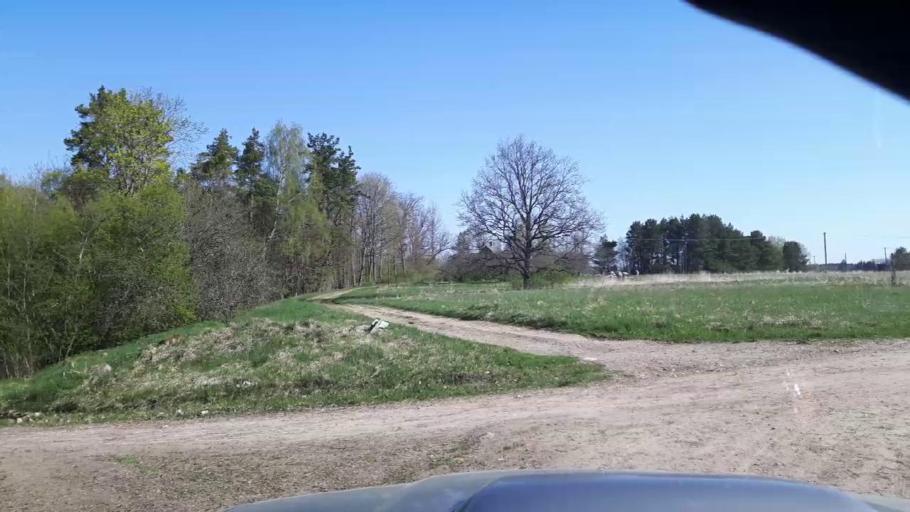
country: EE
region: Paernumaa
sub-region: Sindi linn
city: Sindi
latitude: 58.4552
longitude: 24.7667
